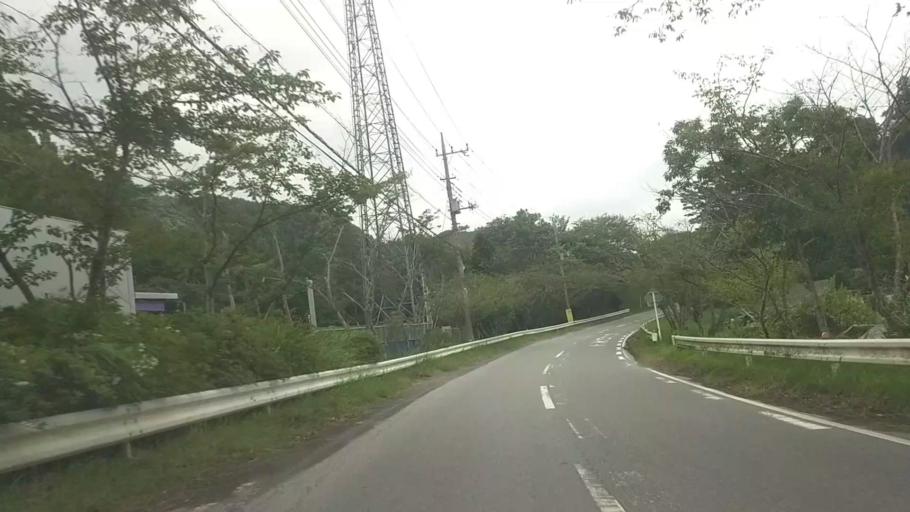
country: JP
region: Chiba
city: Kimitsu
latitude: 35.2274
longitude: 139.9586
